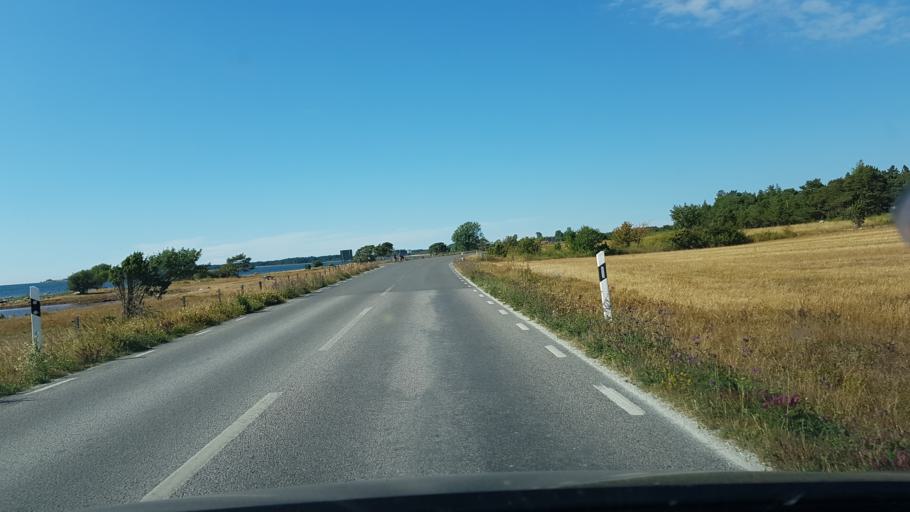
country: SE
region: Gotland
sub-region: Gotland
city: Klintehamn
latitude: 57.4216
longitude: 18.1496
